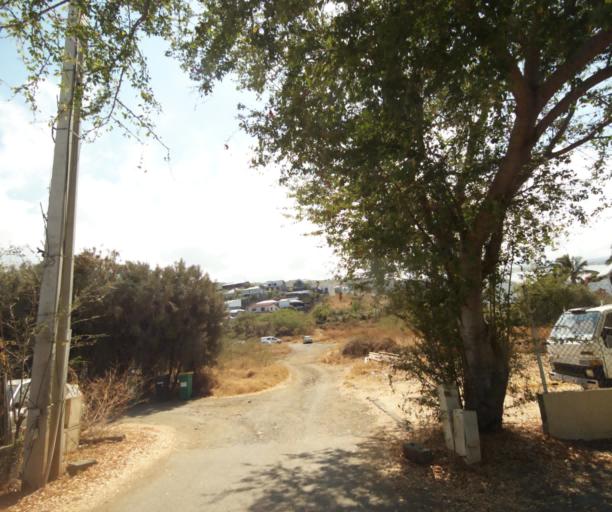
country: RE
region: Reunion
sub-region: Reunion
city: Trois-Bassins
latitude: -21.1001
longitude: 55.2451
